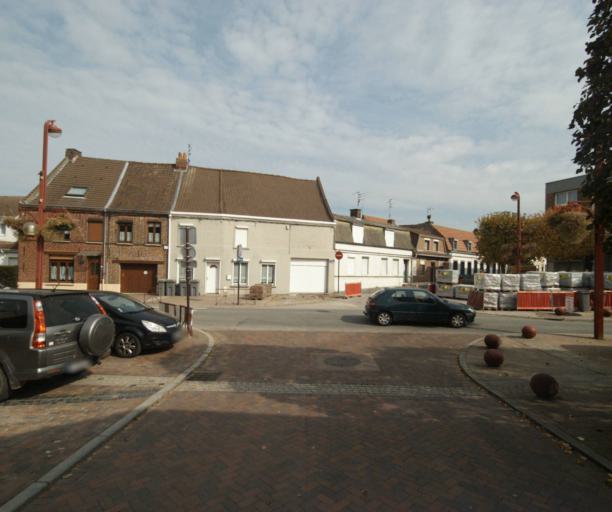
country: FR
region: Nord-Pas-de-Calais
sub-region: Departement du Nord
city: Templemars
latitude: 50.5708
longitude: 3.0542
